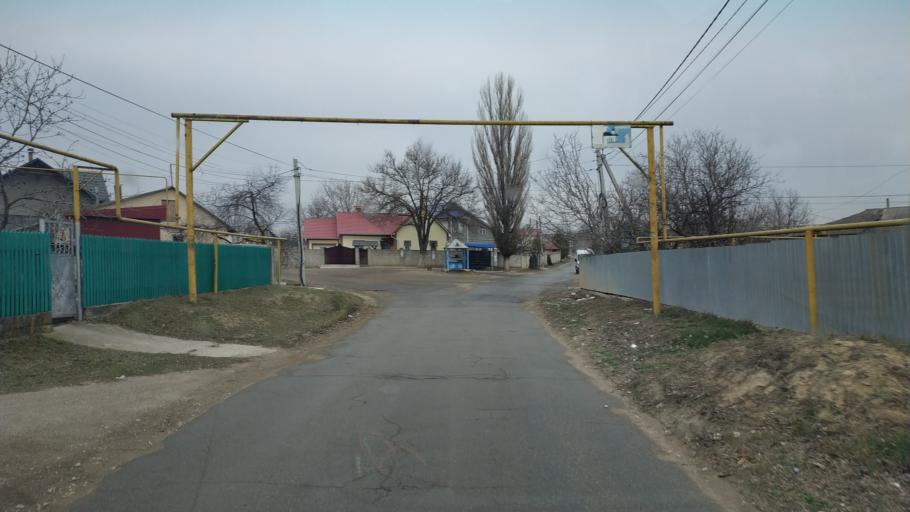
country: MD
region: Chisinau
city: Singera
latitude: 46.9083
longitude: 28.9441
